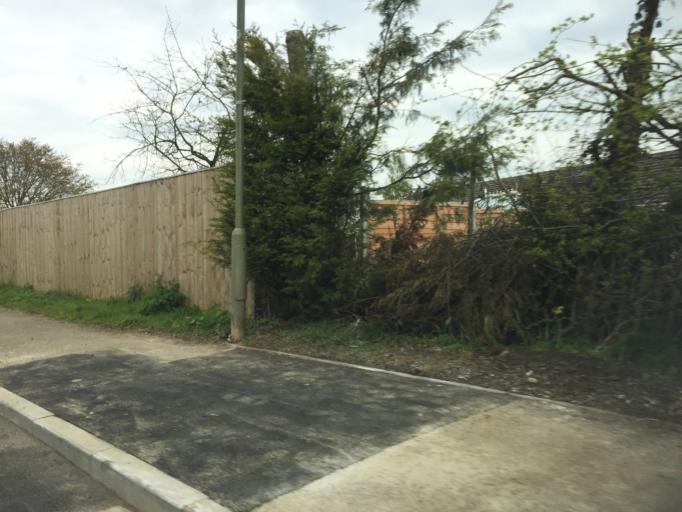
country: GB
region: England
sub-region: Oxfordshire
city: Bicester
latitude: 51.9084
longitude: -1.1733
